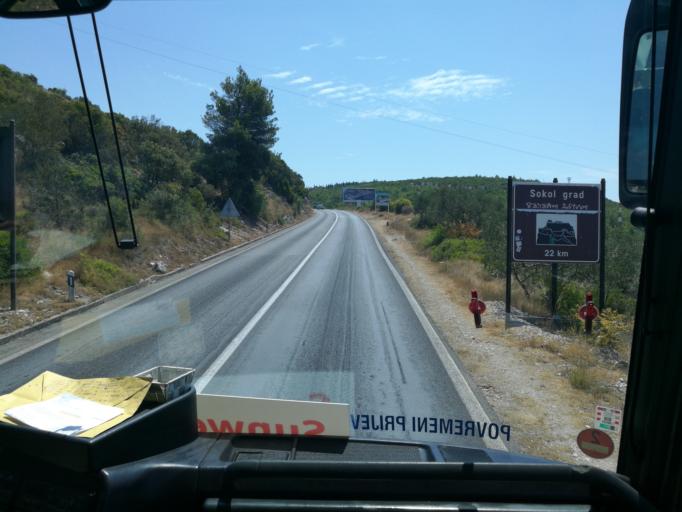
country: HR
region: Dubrovacko-Neretvanska
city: Cavtat
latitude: 42.5754
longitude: 18.2397
